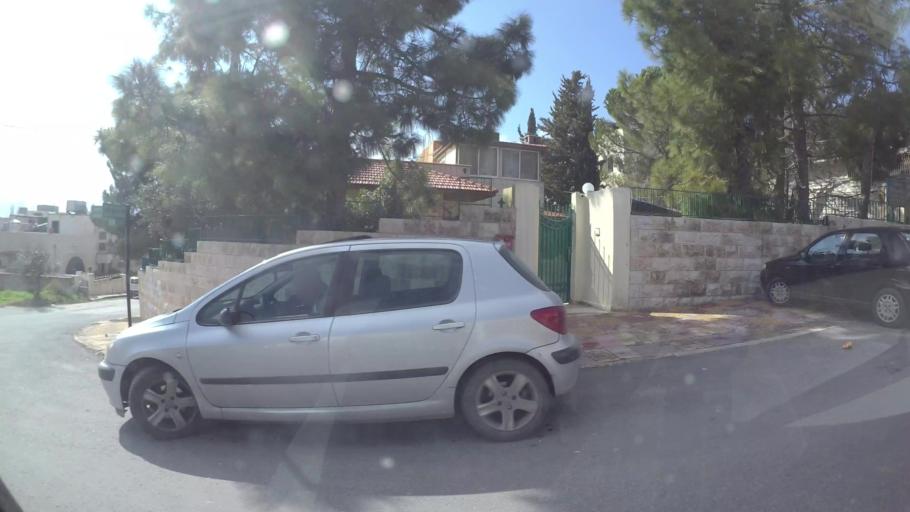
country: JO
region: Amman
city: Al Jubayhah
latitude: 32.0189
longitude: 35.8539
